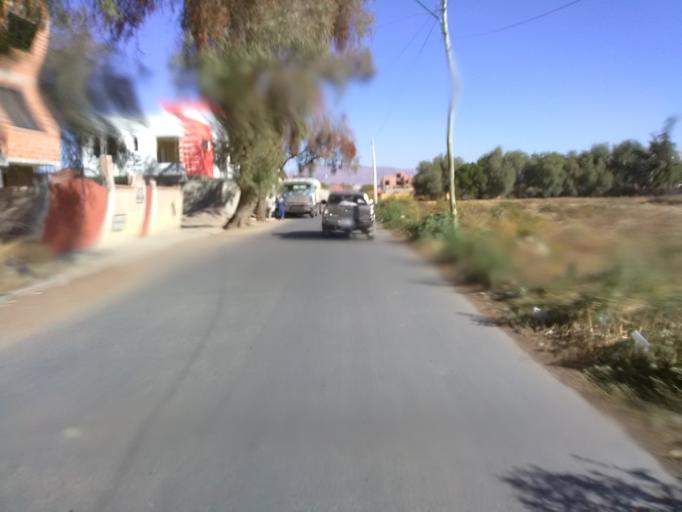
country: BO
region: Cochabamba
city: Cochabamba
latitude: -17.3797
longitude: -66.2008
